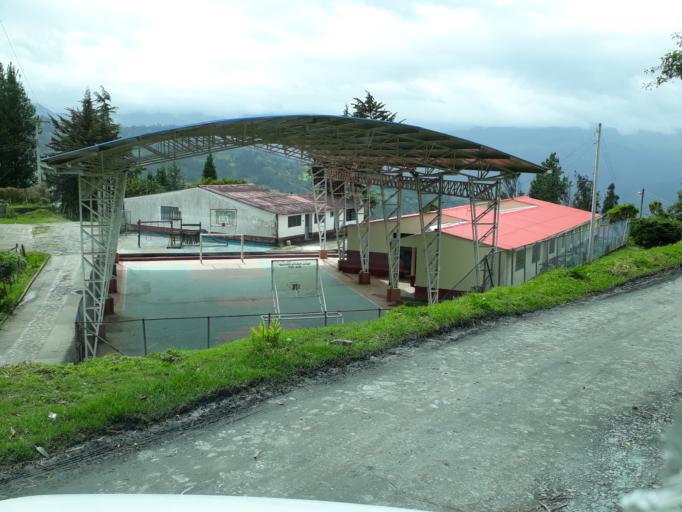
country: CO
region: Cundinamarca
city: Junin
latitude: 4.7634
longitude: -73.6269
